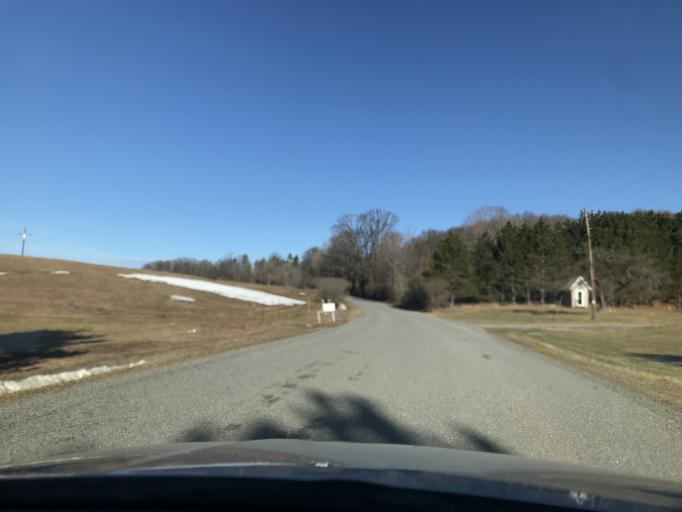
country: US
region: Wisconsin
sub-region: Marinette County
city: Niagara
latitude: 45.3799
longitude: -88.0354
